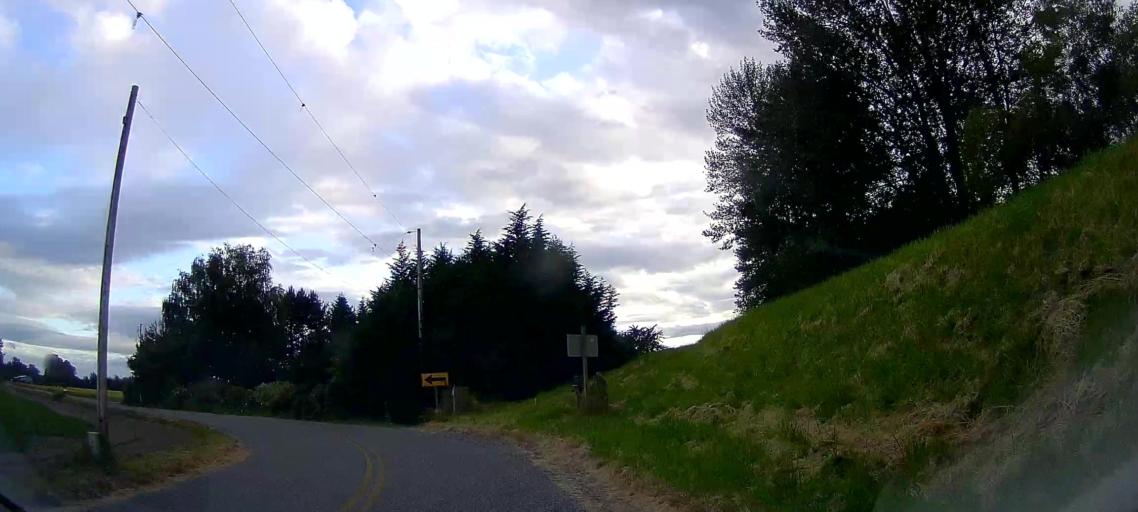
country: US
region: Washington
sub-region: Skagit County
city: Mount Vernon
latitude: 48.3797
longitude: -122.3787
